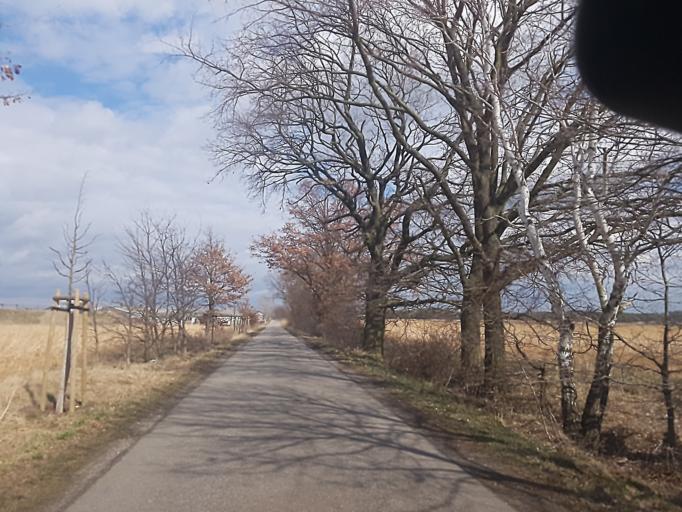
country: DE
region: Brandenburg
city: Ruckersdorf
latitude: 51.5851
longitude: 13.5368
